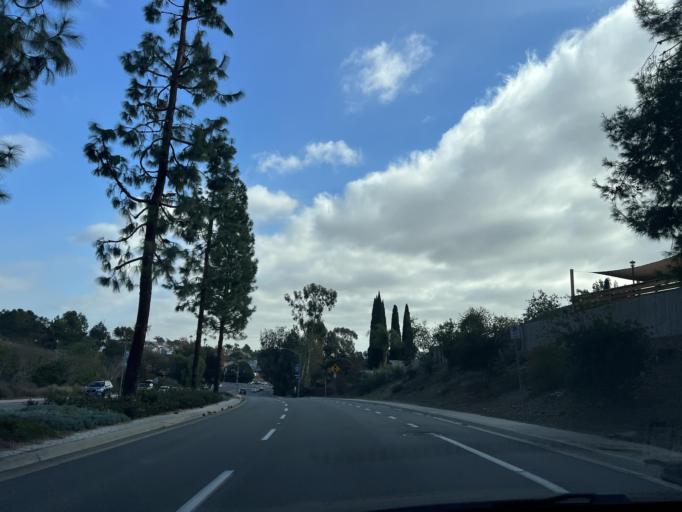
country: US
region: California
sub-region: San Diego County
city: Fairbanks Ranch
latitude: 32.9654
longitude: -117.1285
